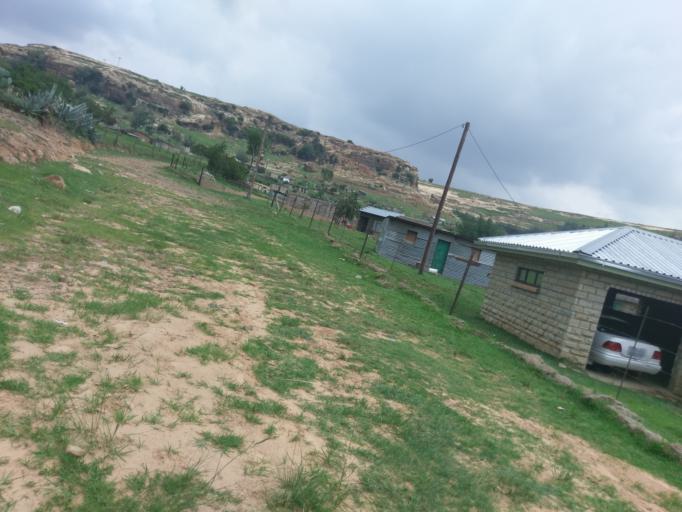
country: LS
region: Leribe
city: Leribe
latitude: -29.0317
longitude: 28.0217
